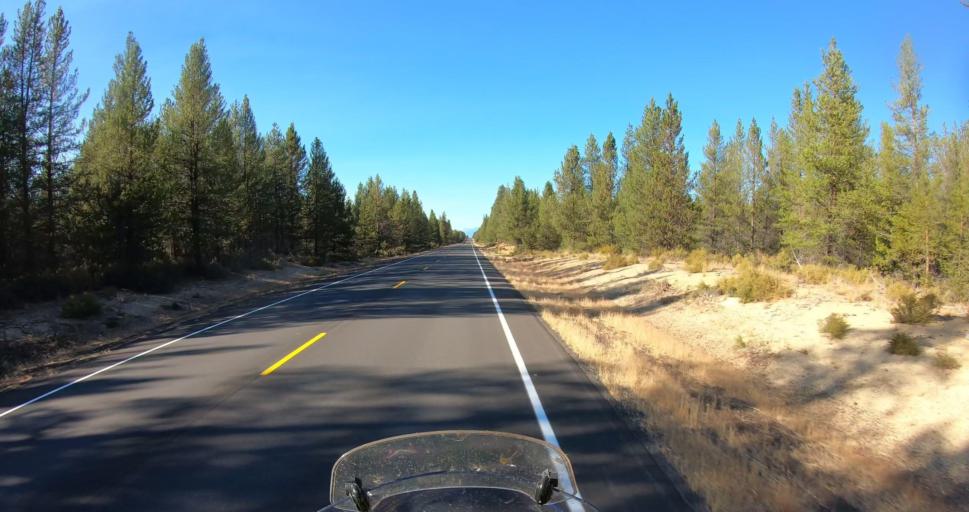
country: US
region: Oregon
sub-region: Deschutes County
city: La Pine
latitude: 43.5312
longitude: -121.4614
